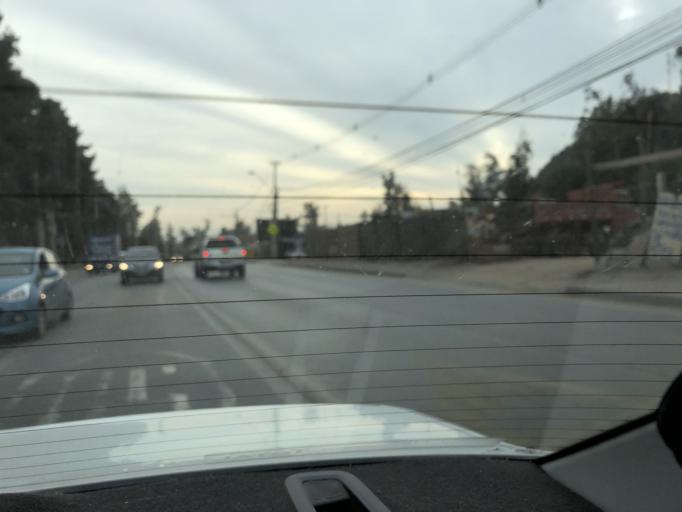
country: CL
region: Santiago Metropolitan
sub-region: Provincia de Cordillera
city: Puente Alto
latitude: -33.5987
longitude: -70.5269
